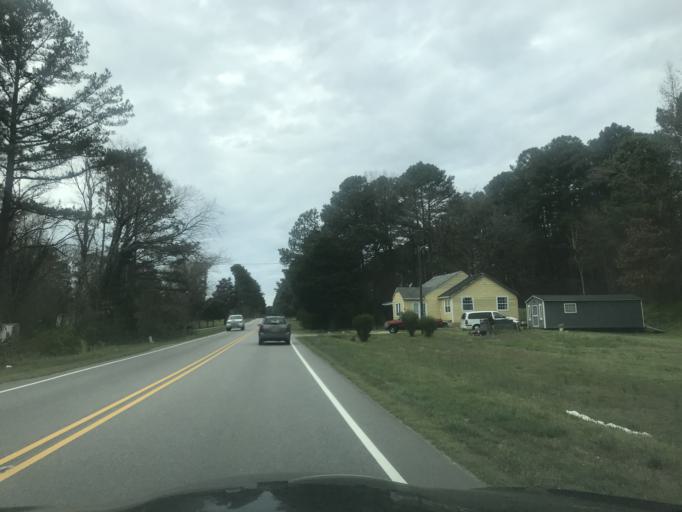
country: US
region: North Carolina
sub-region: Franklin County
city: Franklinton
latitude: 36.0971
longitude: -78.4205
